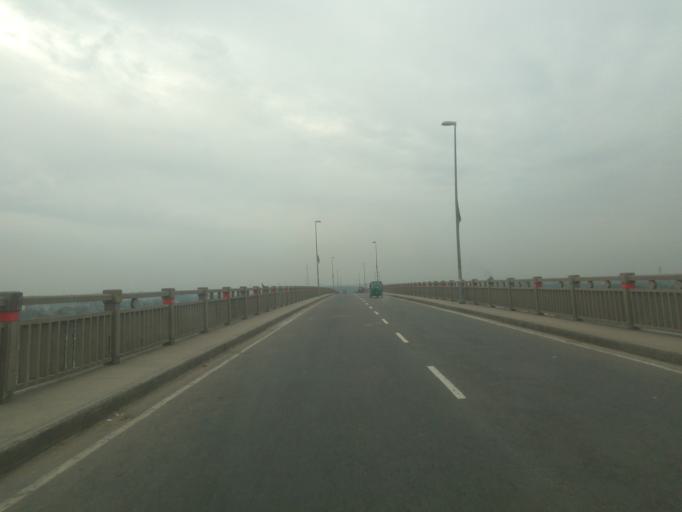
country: BD
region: Dhaka
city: Narayanganj
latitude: 23.5696
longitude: 90.5124
